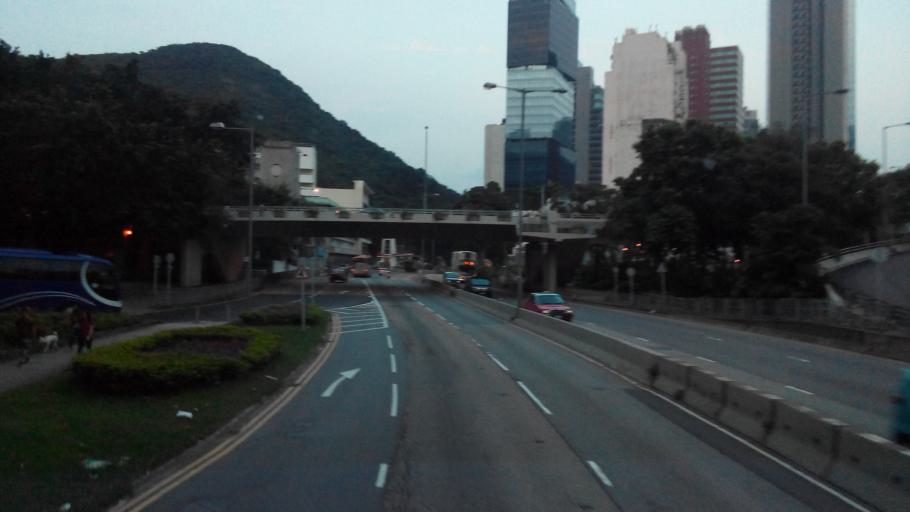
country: HK
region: Central and Western
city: Central
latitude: 22.2480
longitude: 114.1600
